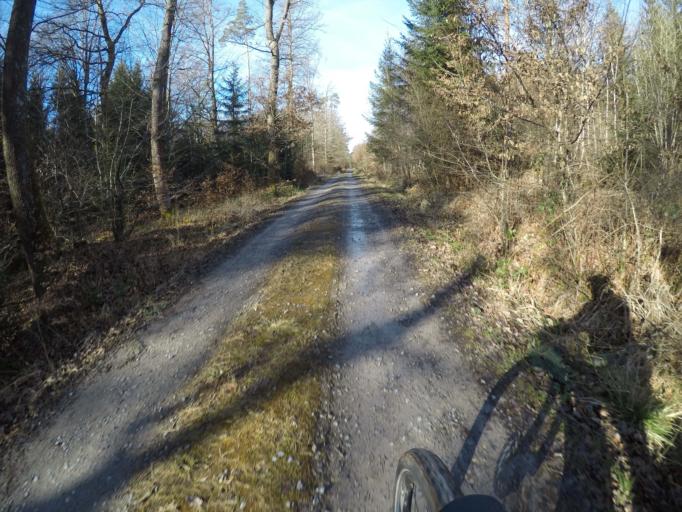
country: DE
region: Baden-Wuerttemberg
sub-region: Regierungsbezirk Stuttgart
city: Steinenbronn
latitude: 48.6875
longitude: 9.0918
